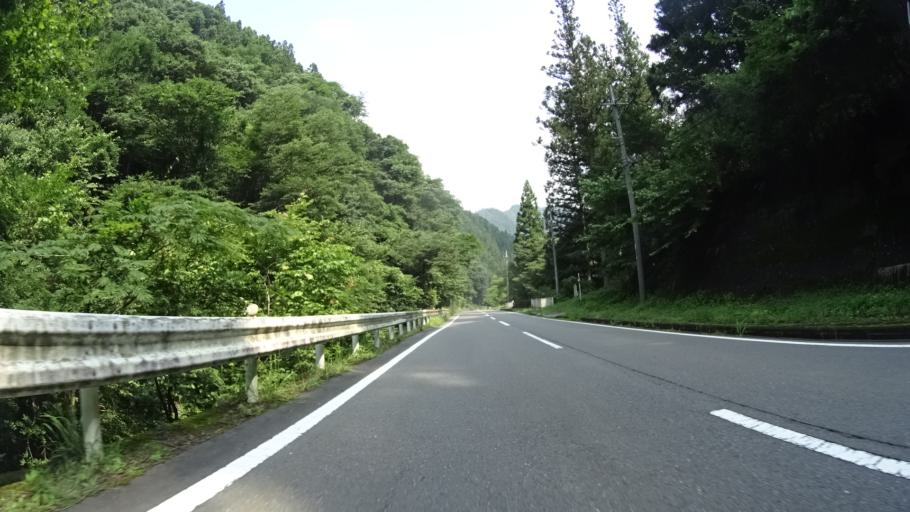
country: JP
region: Gunma
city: Tomioka
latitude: 36.0757
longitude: 138.8260
